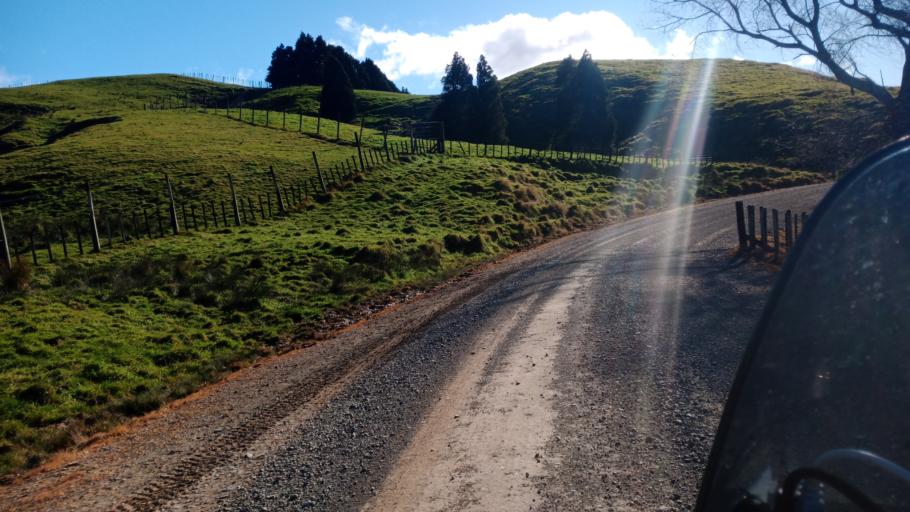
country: NZ
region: Hawke's Bay
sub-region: Wairoa District
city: Wairoa
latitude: -38.7642
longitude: 177.2628
